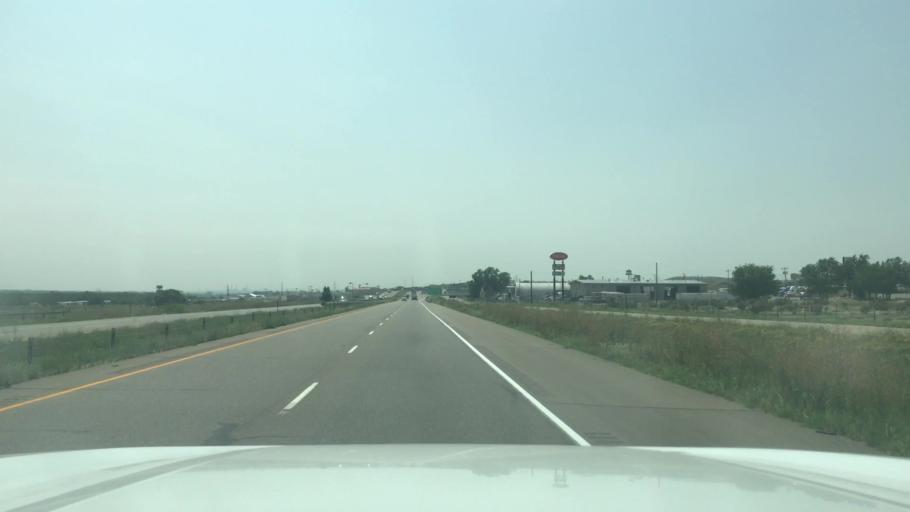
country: US
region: Colorado
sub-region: Pueblo County
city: Pueblo
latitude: 38.3508
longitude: -104.6203
